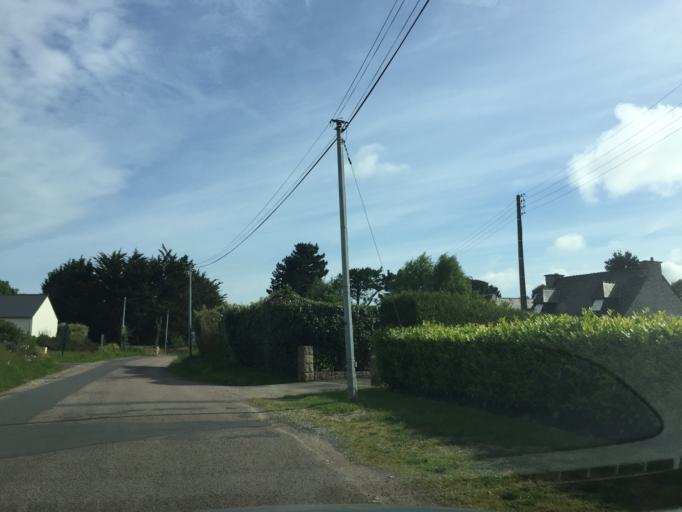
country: FR
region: Brittany
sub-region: Departement des Cotes-d'Armor
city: Matignon
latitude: 48.6340
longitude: -2.3242
